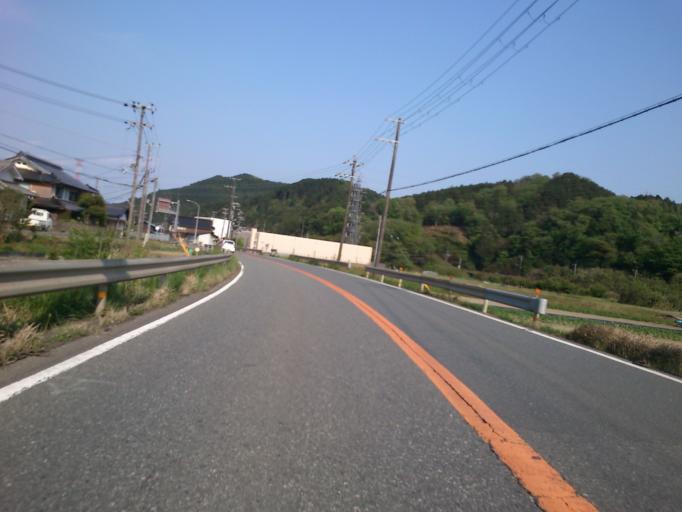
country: JP
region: Kyoto
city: Fukuchiyama
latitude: 35.3214
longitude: 135.0216
